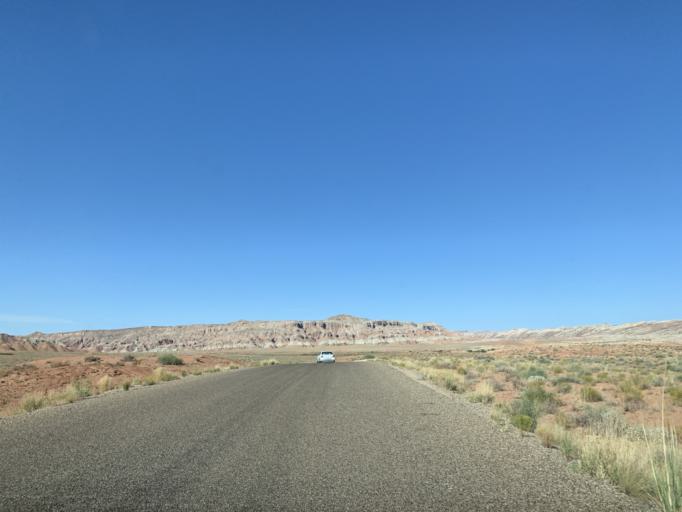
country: US
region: Utah
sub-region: Emery County
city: Ferron
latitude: 38.5800
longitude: -110.7296
